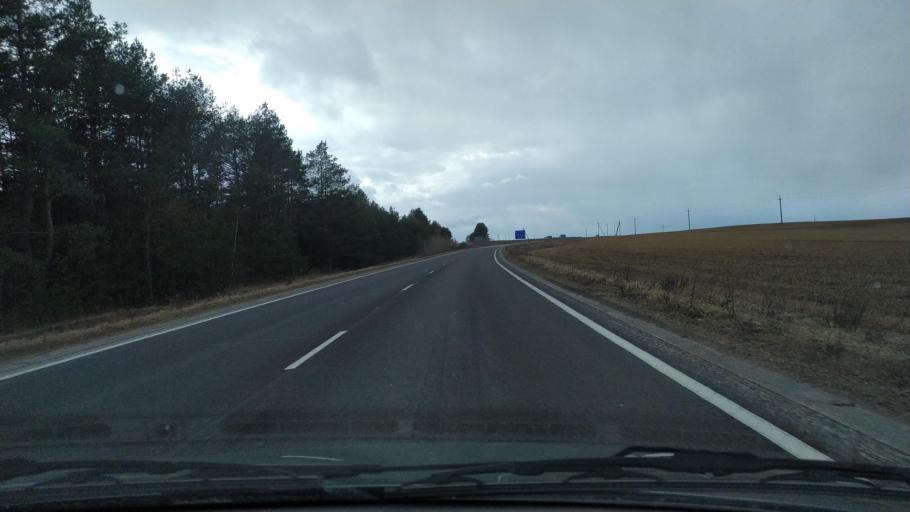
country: BY
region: Brest
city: Kamyanyets
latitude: 52.4012
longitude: 23.8745
